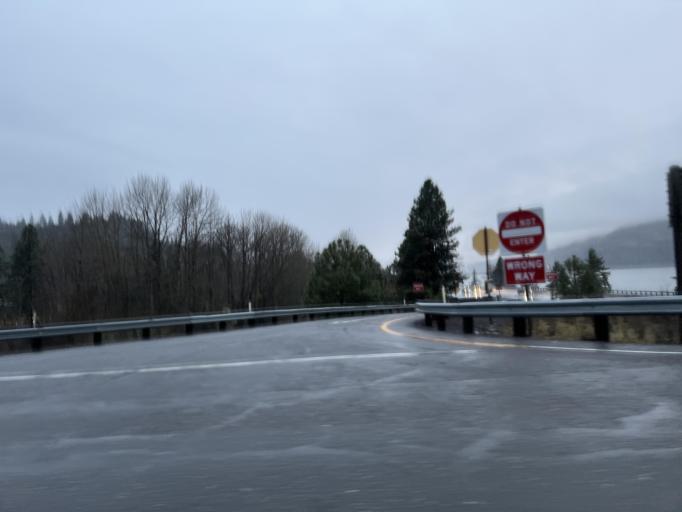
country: US
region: Washington
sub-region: Klickitat County
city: White Salmon
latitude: 45.6855
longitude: -121.4015
